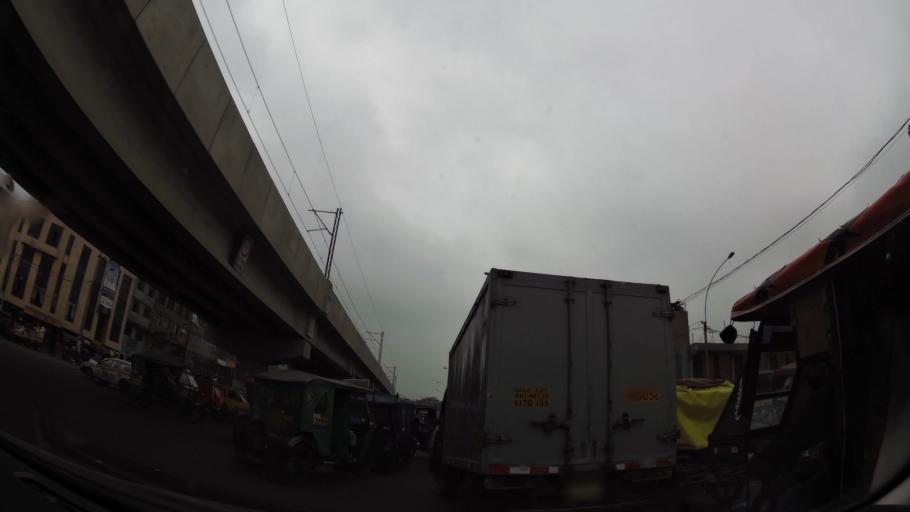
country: PE
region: Lima
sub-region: Lima
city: San Luis
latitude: -12.0625
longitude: -77.0126
